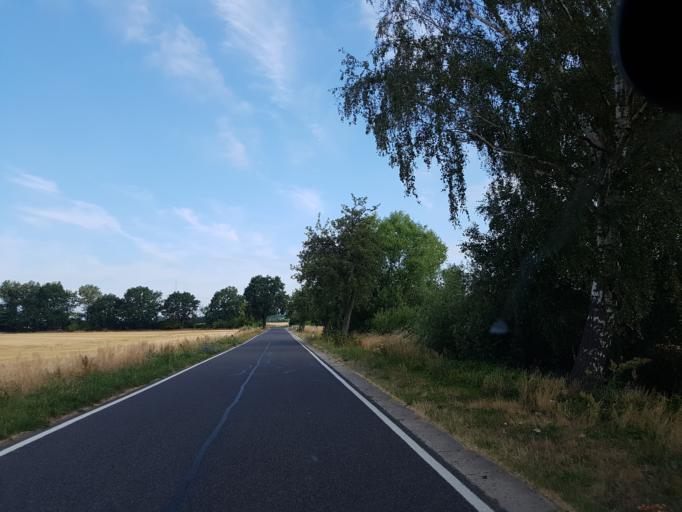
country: DE
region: Brandenburg
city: Luckau
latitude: 51.8437
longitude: 13.6287
